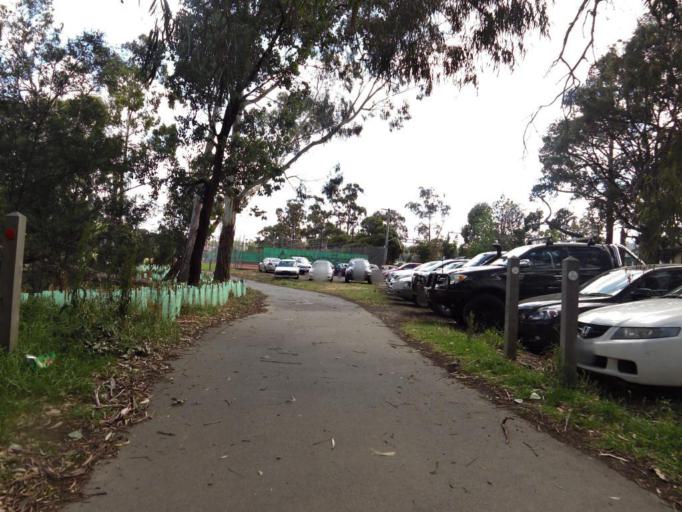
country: AU
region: Victoria
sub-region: Nillumbik
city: Eltham North
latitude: -37.7141
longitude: 145.1460
